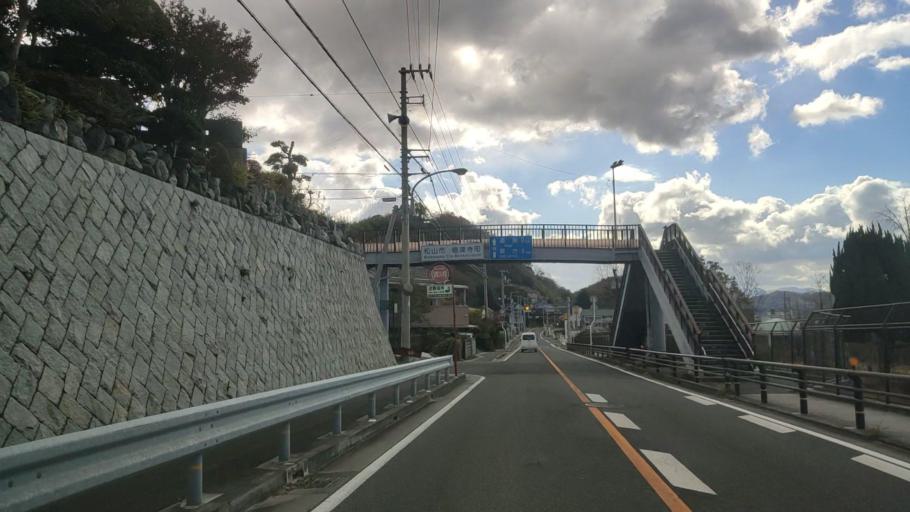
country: JP
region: Ehime
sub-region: Shikoku-chuo Shi
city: Matsuyama
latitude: 33.8761
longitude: 132.7074
